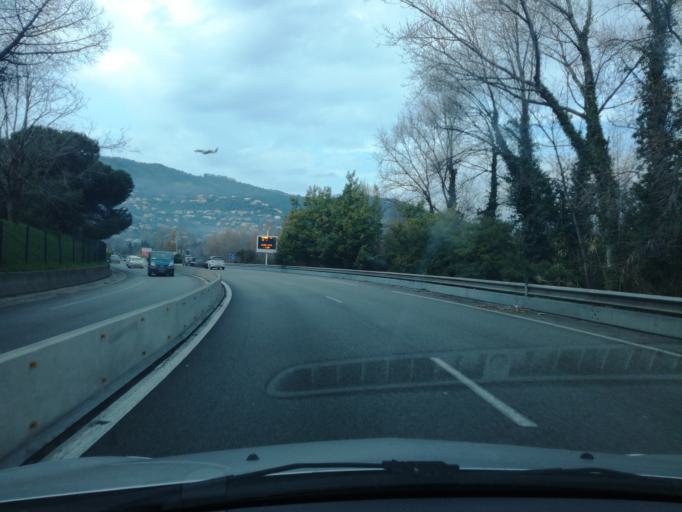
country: FR
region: Provence-Alpes-Cote d'Azur
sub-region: Departement des Alpes-Maritimes
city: Mandelieu-la-Napoule
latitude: 43.5611
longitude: 6.9530
